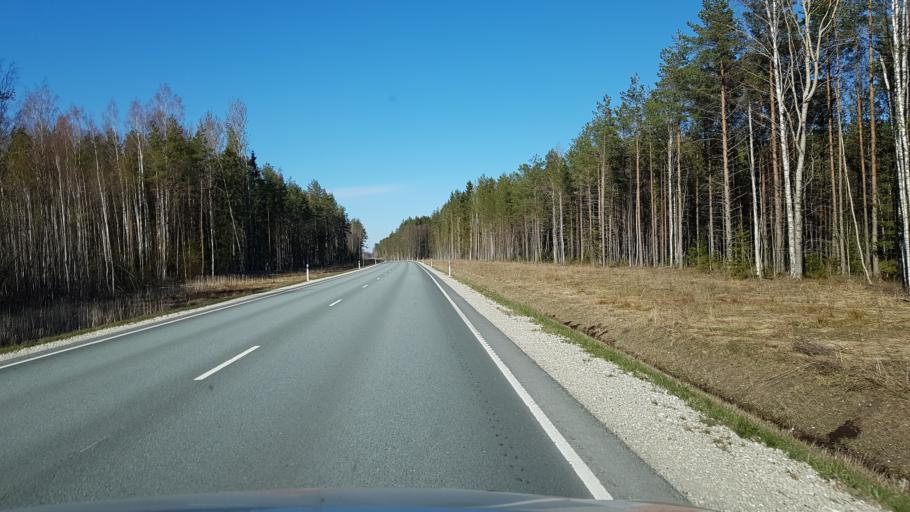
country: EE
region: Jogevamaa
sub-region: Mustvee linn
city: Mustvee
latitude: 58.8671
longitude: 26.9376
